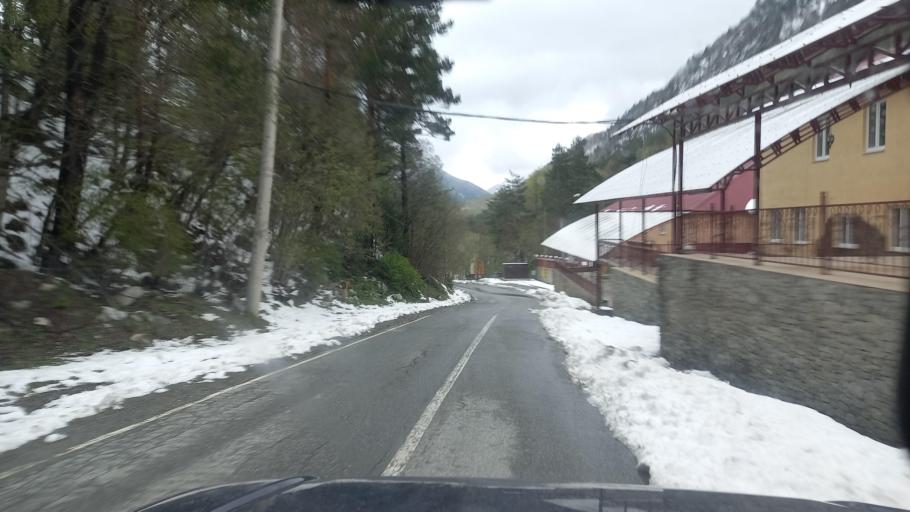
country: RU
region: North Ossetia
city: Mizur
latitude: 42.7914
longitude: 43.9143
